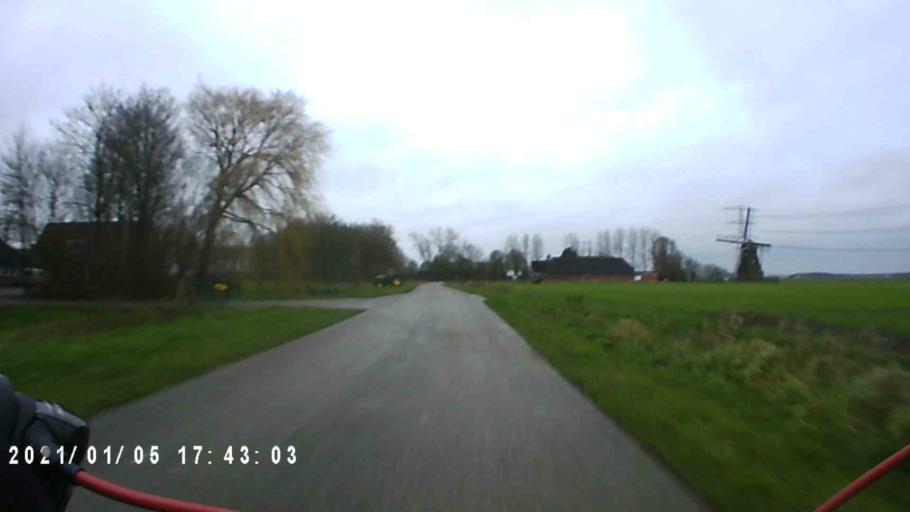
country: NL
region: Groningen
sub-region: Gemeente Slochteren
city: Slochteren
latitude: 53.2154
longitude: 6.9071
